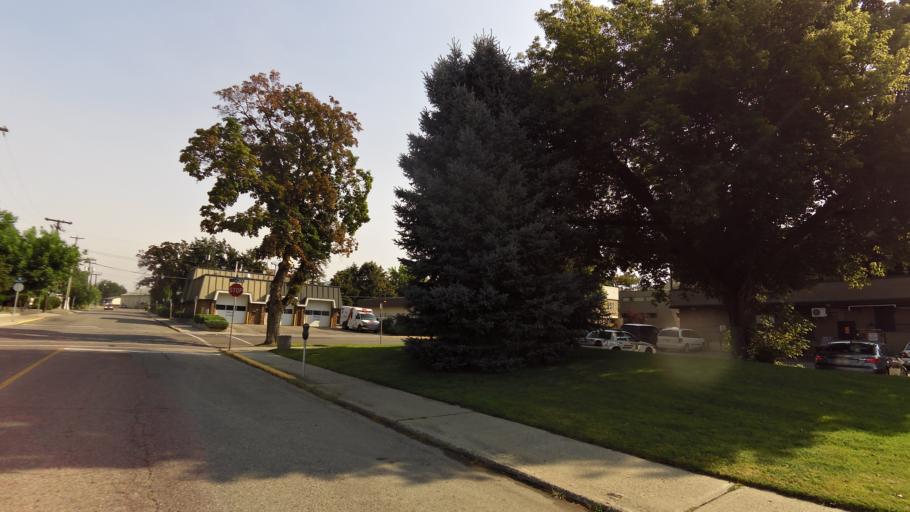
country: CA
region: British Columbia
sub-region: Regional District of North Okanagan
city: Vernon
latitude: 50.2671
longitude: -119.2723
